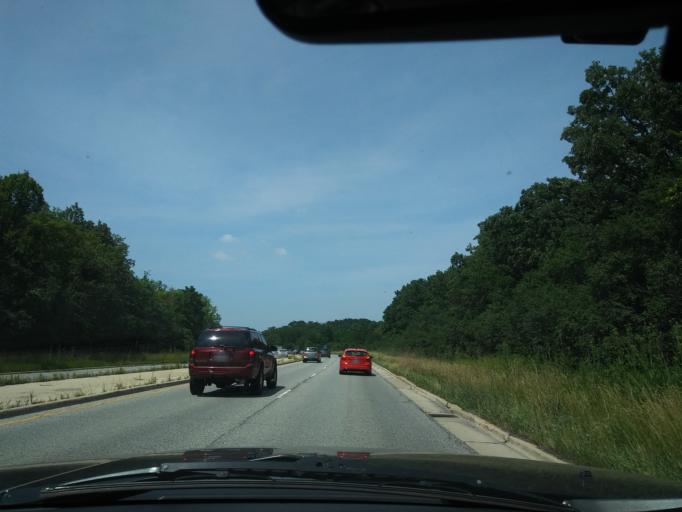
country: US
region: Illinois
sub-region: Cook County
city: Palos Heights
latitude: 41.6204
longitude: -87.7947
